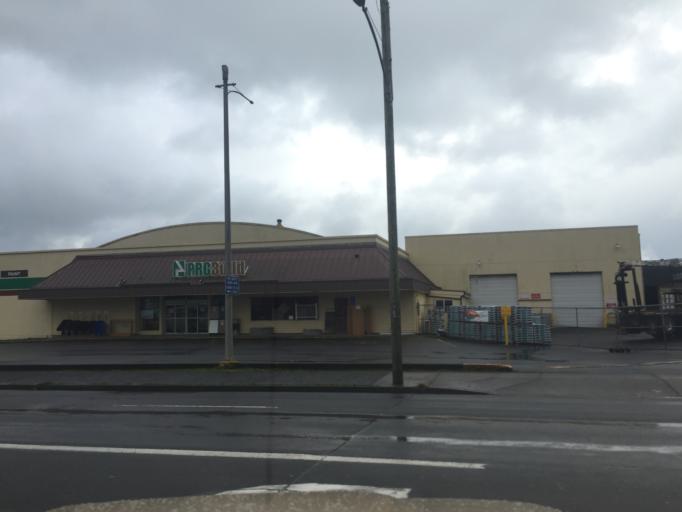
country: US
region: Oregon
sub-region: Lincoln County
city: Newport
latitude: 44.6407
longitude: -124.0530
